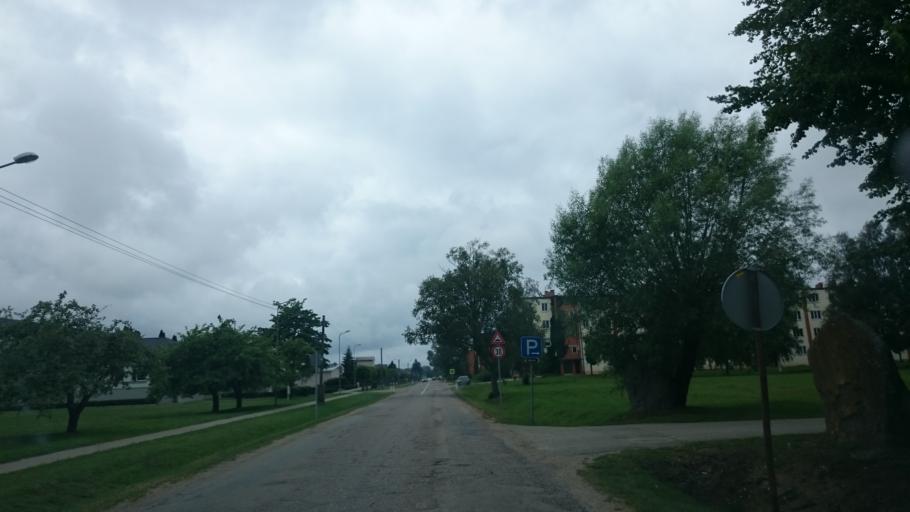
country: LV
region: Pavilostas
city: Pavilosta
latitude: 56.8827
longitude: 21.2051
